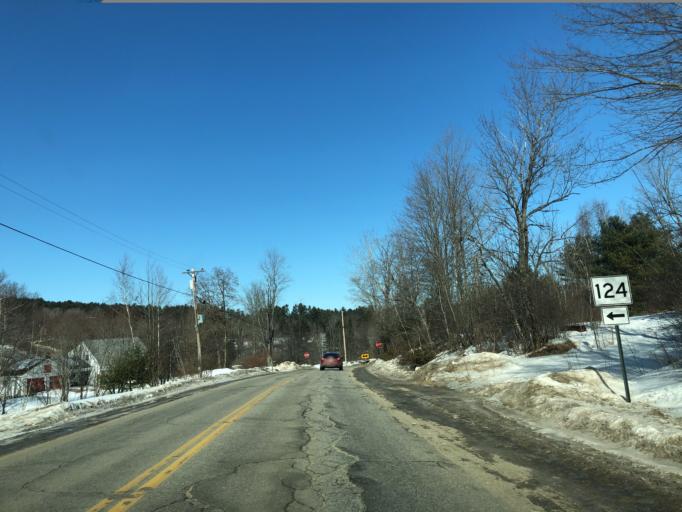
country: US
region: Maine
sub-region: Oxford County
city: Buckfield
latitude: 44.2574
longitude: -70.3374
